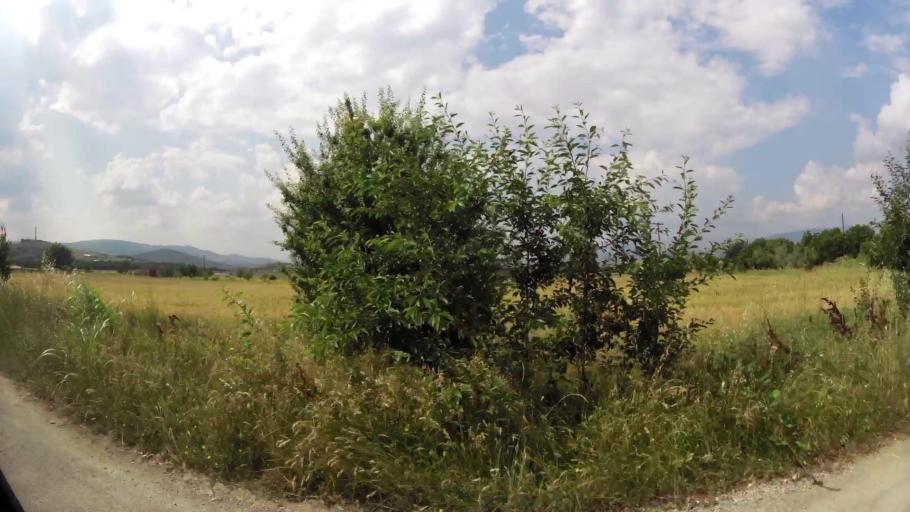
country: GR
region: West Macedonia
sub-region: Nomos Kozanis
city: Koila
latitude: 40.3532
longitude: 21.8335
